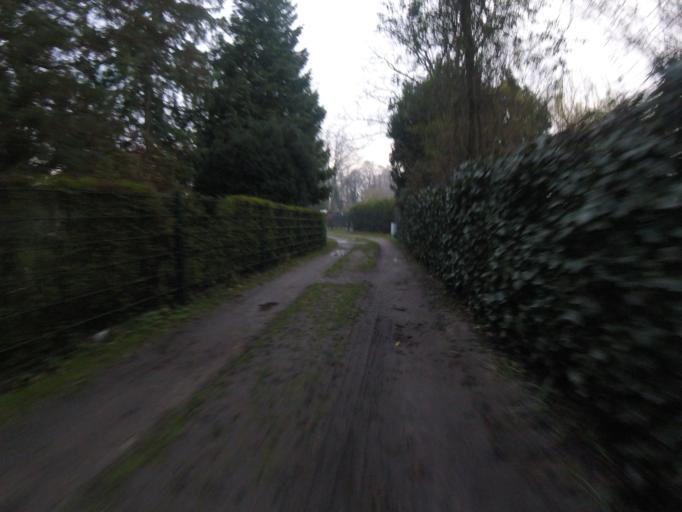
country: DE
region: Brandenburg
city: Konigs Wusterhausen
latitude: 52.2934
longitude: 13.6693
